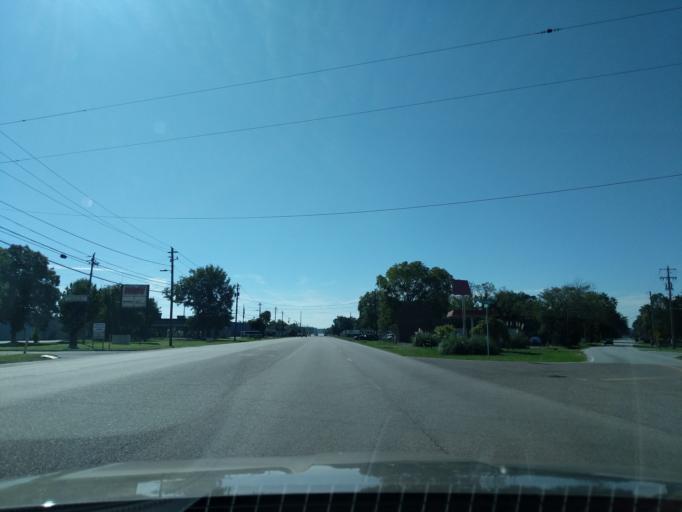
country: US
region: Georgia
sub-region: Richmond County
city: Augusta
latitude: 33.4150
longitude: -82.0069
